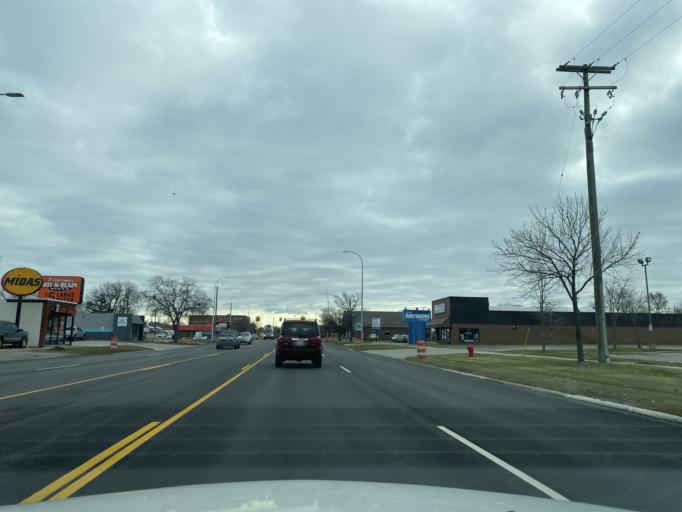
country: US
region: Michigan
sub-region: Wayne County
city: Southgate
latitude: 42.1993
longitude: -83.1864
